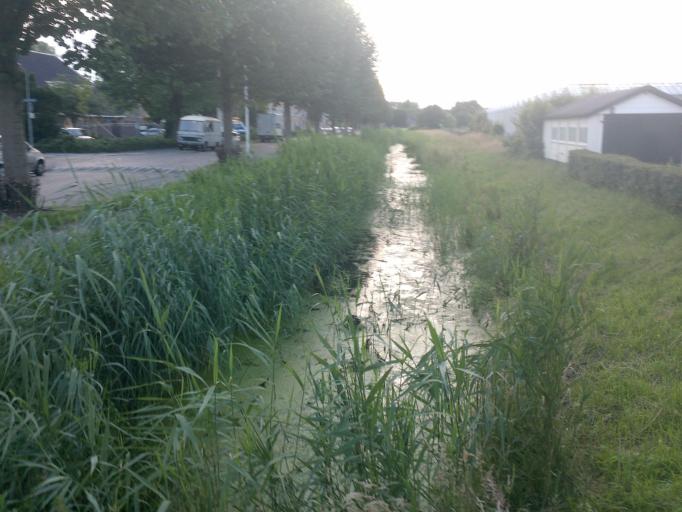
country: NL
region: South Holland
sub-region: Gemeente Wassenaar
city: Wassenaar
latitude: 52.1510
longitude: 4.3964
